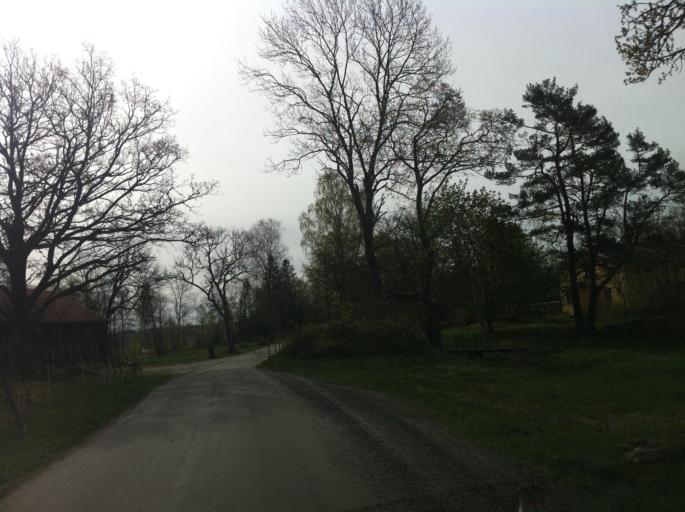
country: SE
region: Vaestra Goetaland
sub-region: Bollebygds Kommun
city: Bollebygd
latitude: 57.7605
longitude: 12.5889
